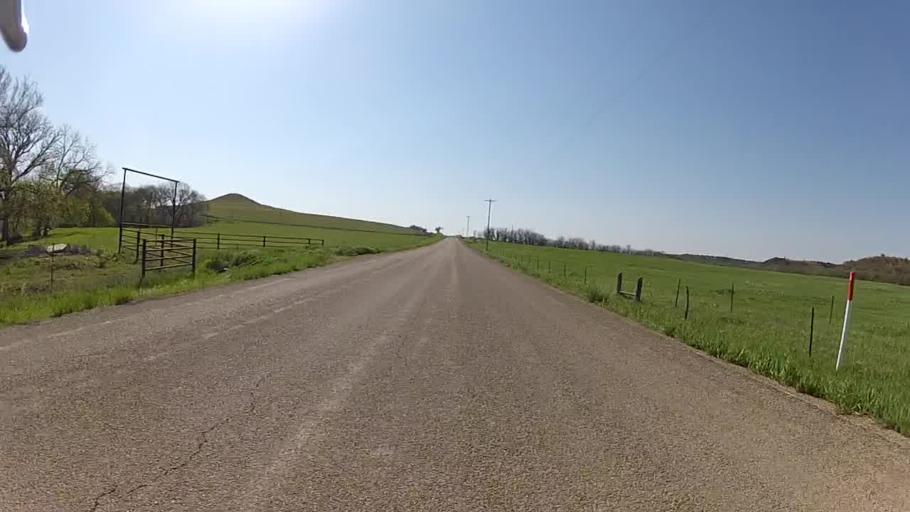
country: US
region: Kansas
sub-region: Riley County
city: Ogden
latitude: 39.0153
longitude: -96.6849
